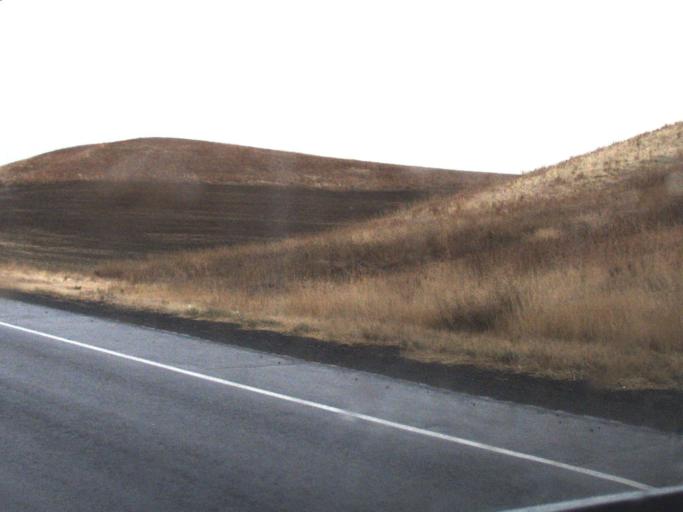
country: US
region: Washington
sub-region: Whitman County
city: Colfax
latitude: 46.9288
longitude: -117.3402
